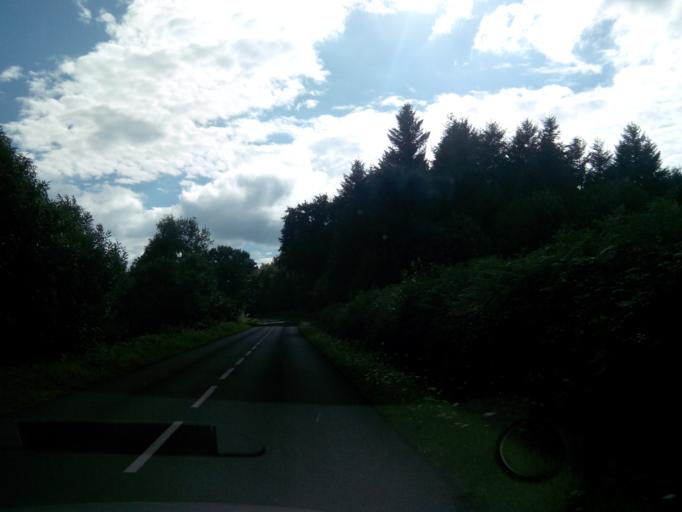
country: FR
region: Limousin
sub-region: Departement de la Haute-Vienne
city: Saint-Leonard-de-Noblat
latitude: 45.8295
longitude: 1.5456
